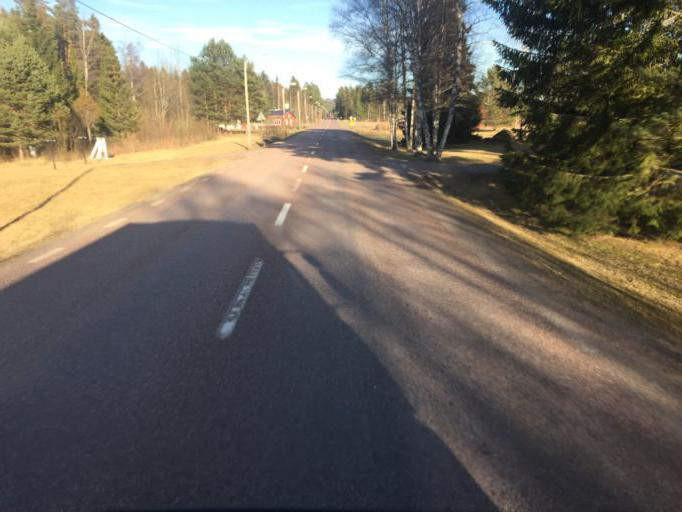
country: SE
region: Dalarna
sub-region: Gagnefs Kommun
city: Mockfjard
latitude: 60.5097
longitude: 14.8131
